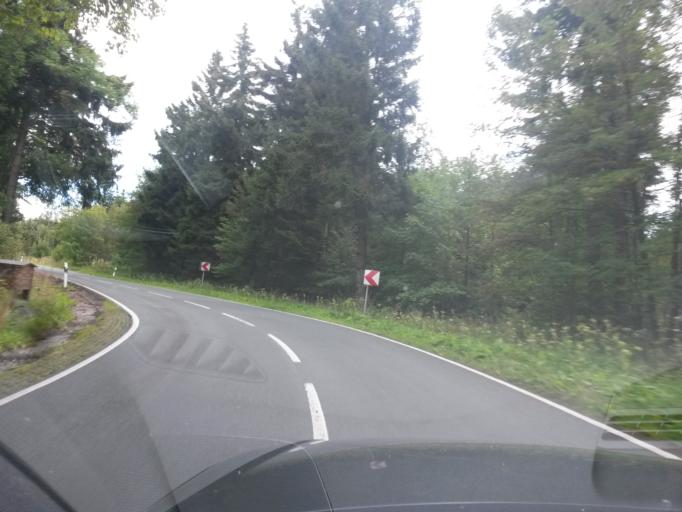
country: DE
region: Thuringia
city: Birx
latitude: 50.5516
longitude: 10.0436
